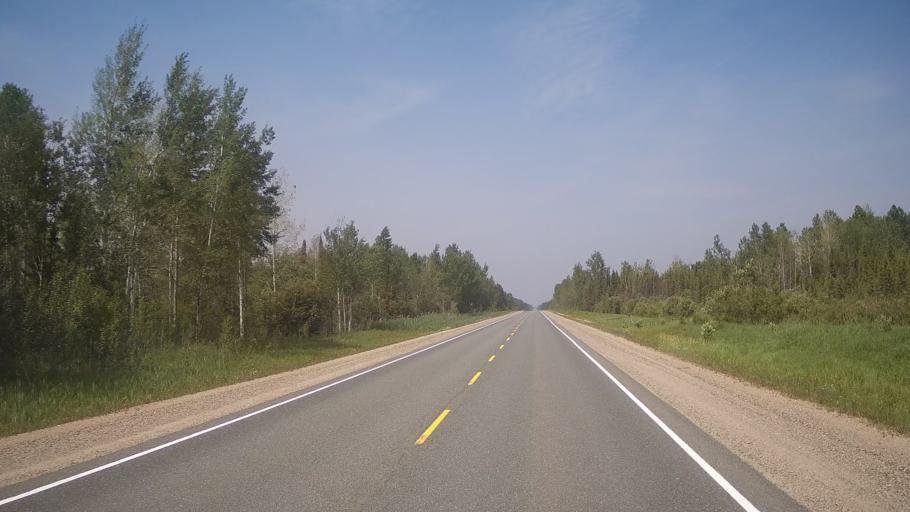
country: CA
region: Ontario
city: Timmins
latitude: 48.8226
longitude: -81.3708
